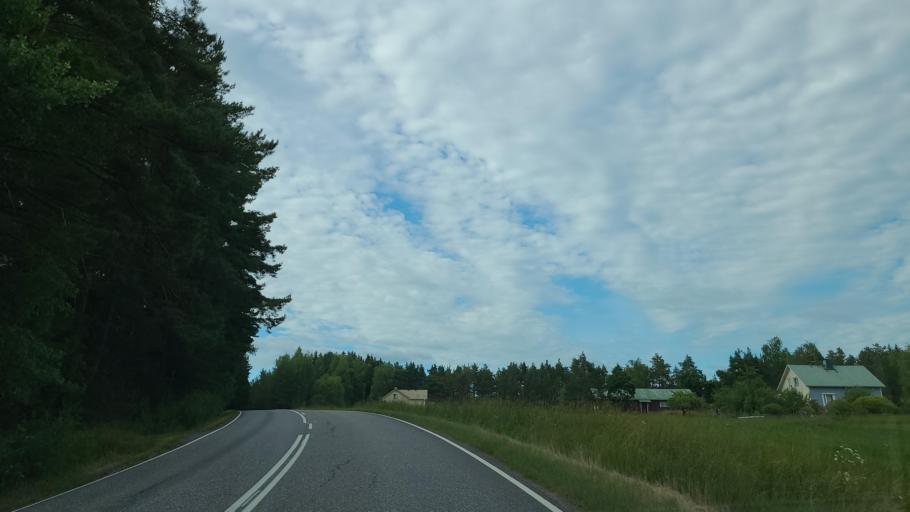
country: FI
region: Varsinais-Suomi
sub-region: Turku
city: Rymaettylae
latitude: 60.3595
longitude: 21.9535
